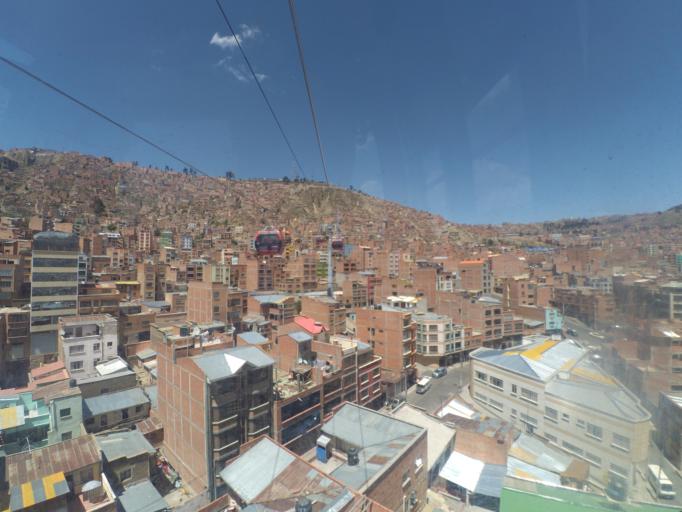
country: BO
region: La Paz
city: La Paz
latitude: -16.4980
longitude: -68.1563
